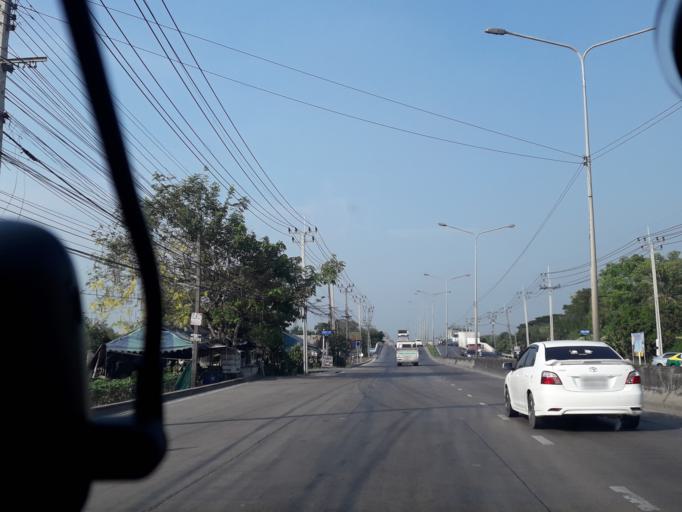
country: TH
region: Bangkok
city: Khlong Sam Wa
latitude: 13.8782
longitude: 100.7317
